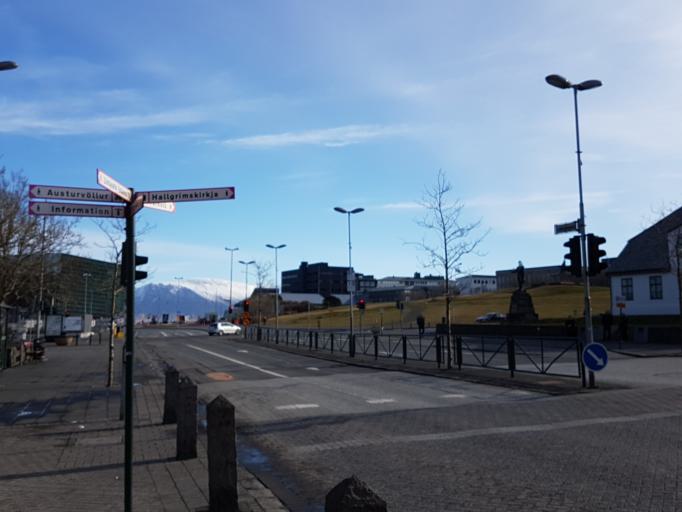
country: IS
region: Capital Region
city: Kopavogur
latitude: 64.1473
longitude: -21.9366
